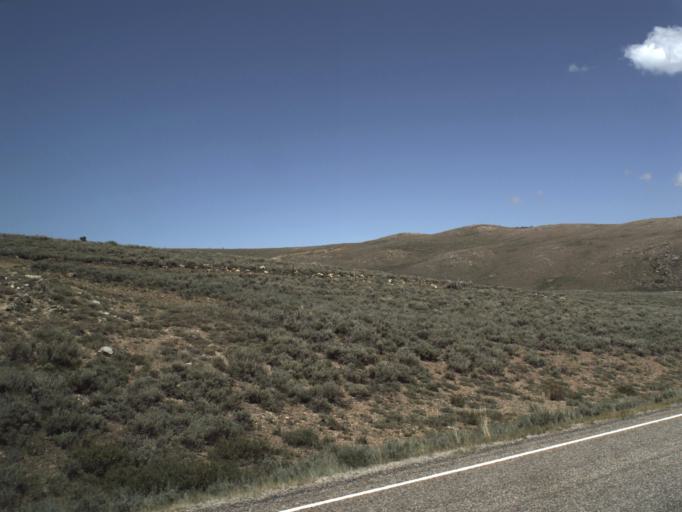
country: US
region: Utah
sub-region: Rich County
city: Randolph
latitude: 41.4829
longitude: -111.4173
